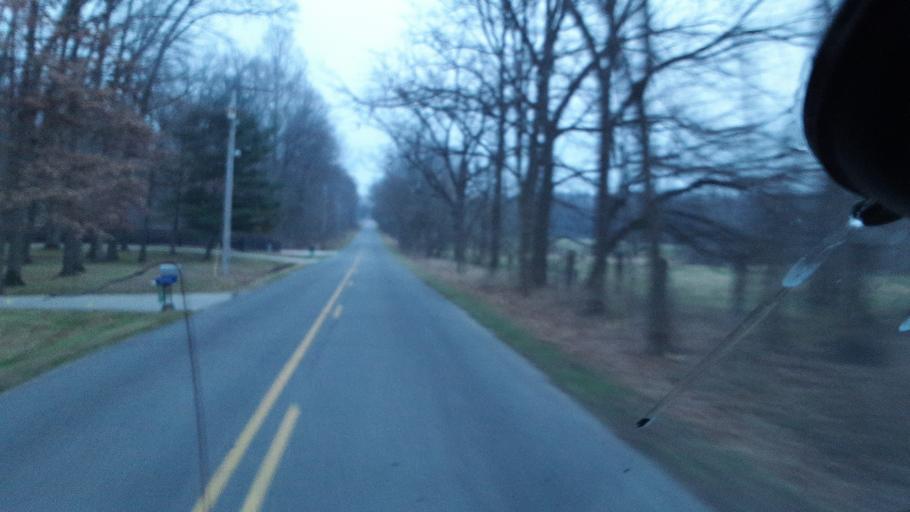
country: US
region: Indiana
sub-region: Elkhart County
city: Bristol
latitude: 41.6614
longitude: -85.7872
